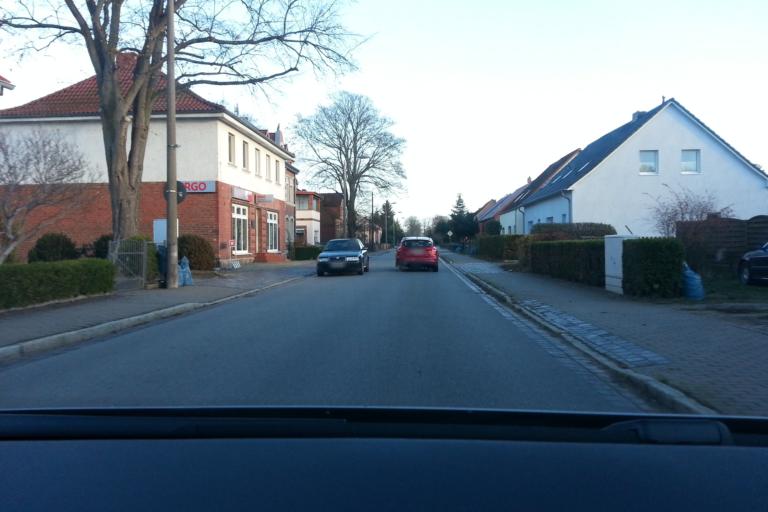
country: DE
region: Mecklenburg-Vorpommern
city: Ferdinandshof
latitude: 53.6645
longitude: 13.8900
